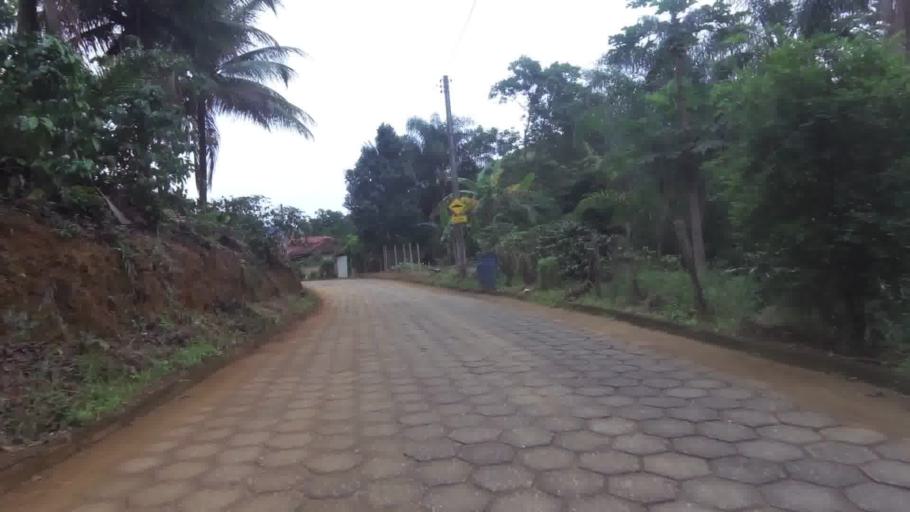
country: BR
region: Espirito Santo
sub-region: Iconha
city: Iconha
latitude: -20.7712
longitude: -40.8301
